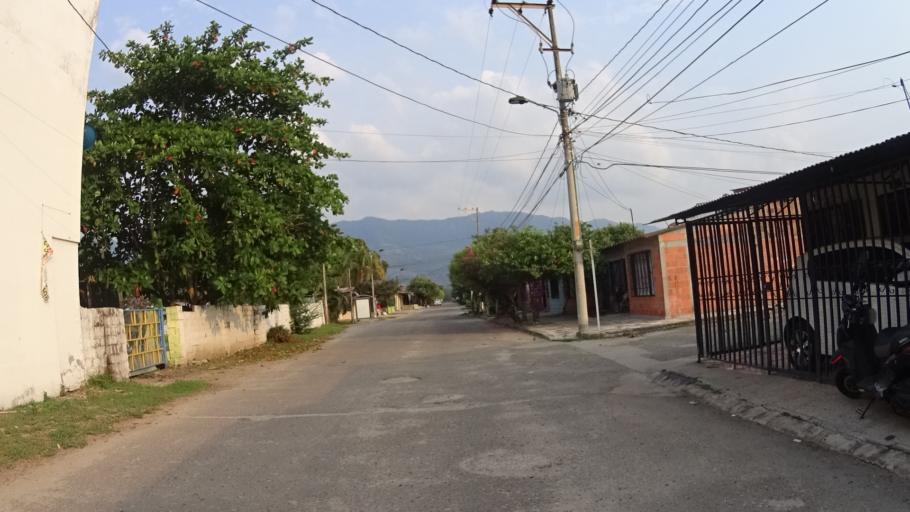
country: CO
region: Caldas
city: La Dorada
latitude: 5.4433
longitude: -74.6566
